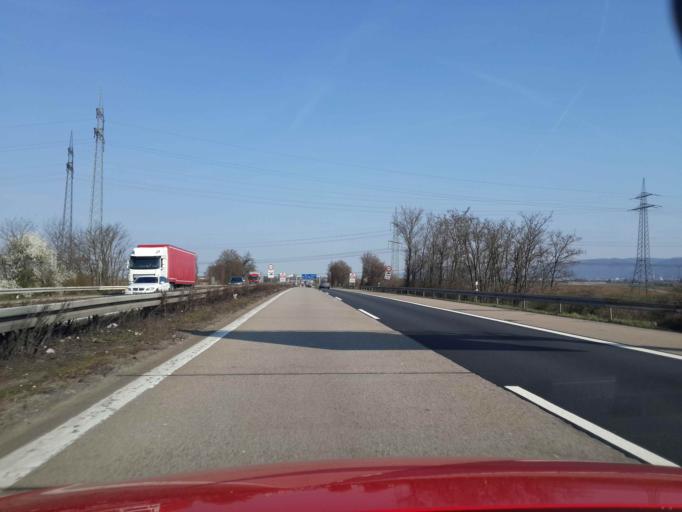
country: DE
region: Baden-Wuerttemberg
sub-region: Karlsruhe Region
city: Sandhausen
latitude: 49.3549
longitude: 8.6316
